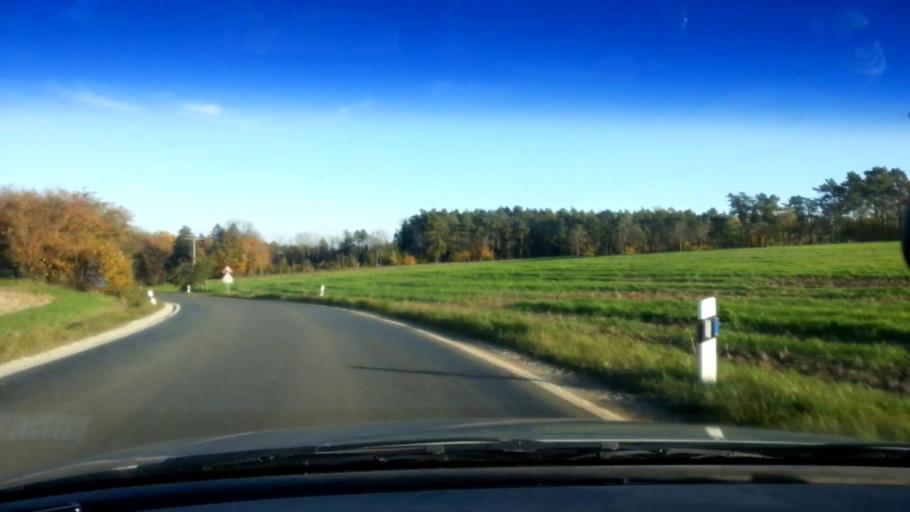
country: DE
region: Bavaria
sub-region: Upper Franconia
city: Poxdorf
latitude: 49.8955
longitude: 11.0936
